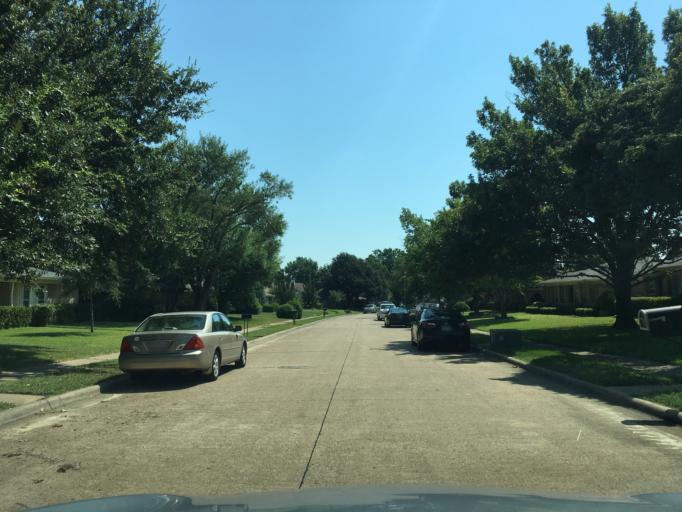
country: US
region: Texas
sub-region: Dallas County
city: Garland
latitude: 32.9356
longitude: -96.6521
